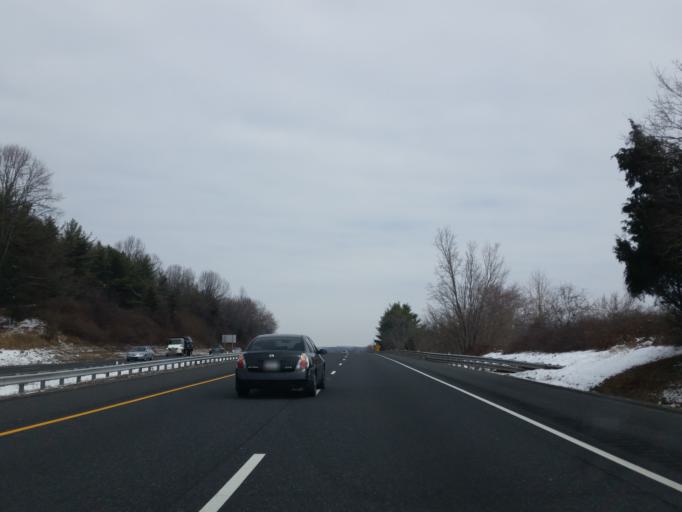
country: US
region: Maryland
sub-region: Baltimore County
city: Hunt Valley
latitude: 39.5989
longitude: -76.6627
